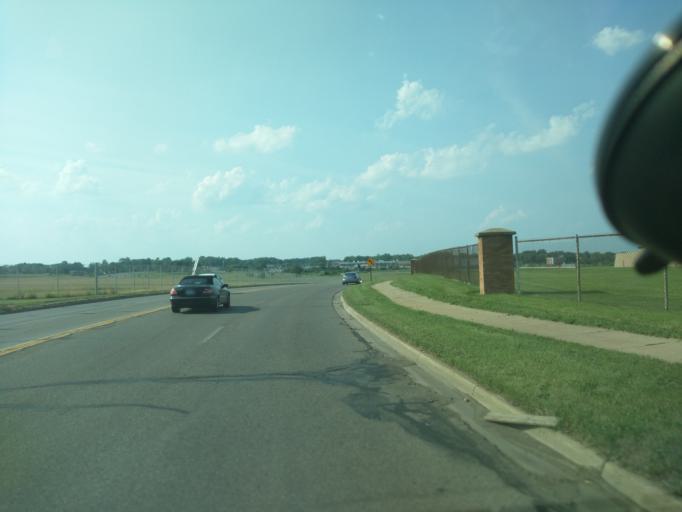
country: US
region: Michigan
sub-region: Jackson County
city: Jackson
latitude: 42.2622
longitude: -84.4483
